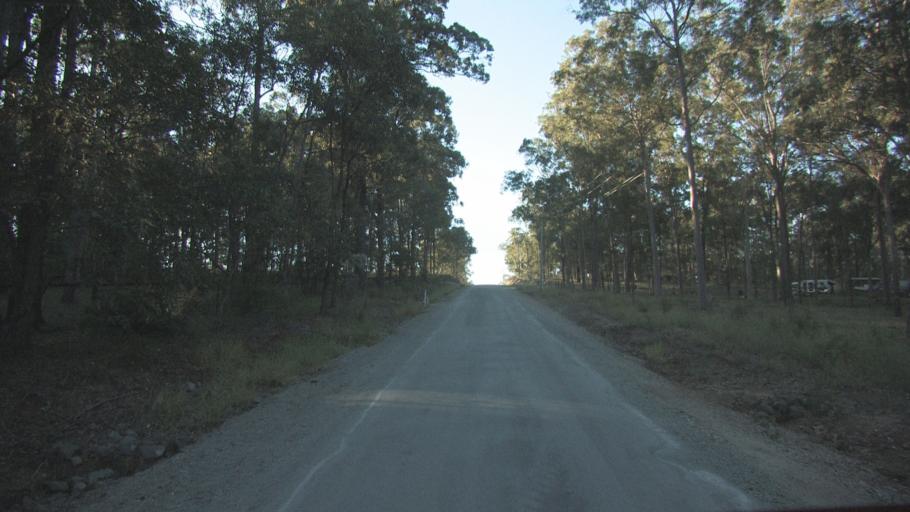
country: AU
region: Queensland
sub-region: Logan
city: Chambers Flat
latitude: -27.7671
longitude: 153.1328
